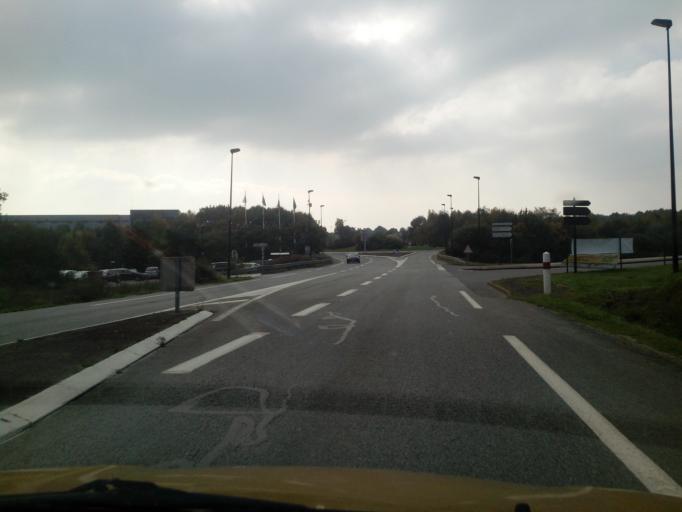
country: FR
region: Brittany
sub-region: Departement du Morbihan
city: Ploermel
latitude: 47.9203
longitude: -2.3867
